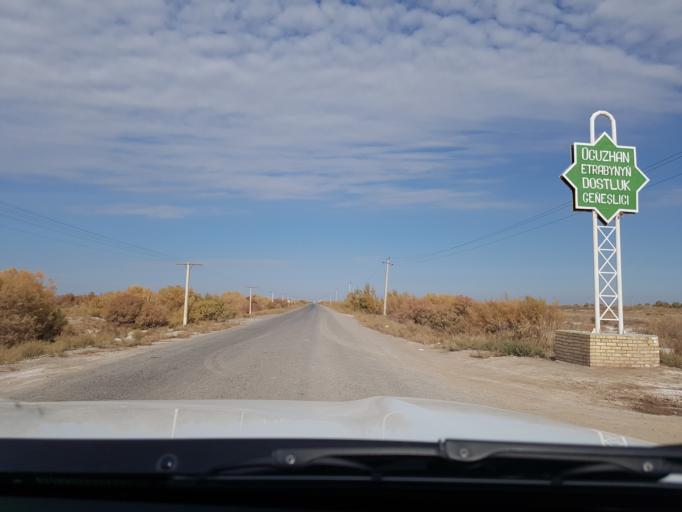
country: TM
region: Ahal
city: Tejen
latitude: 37.3491
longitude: 61.0918
